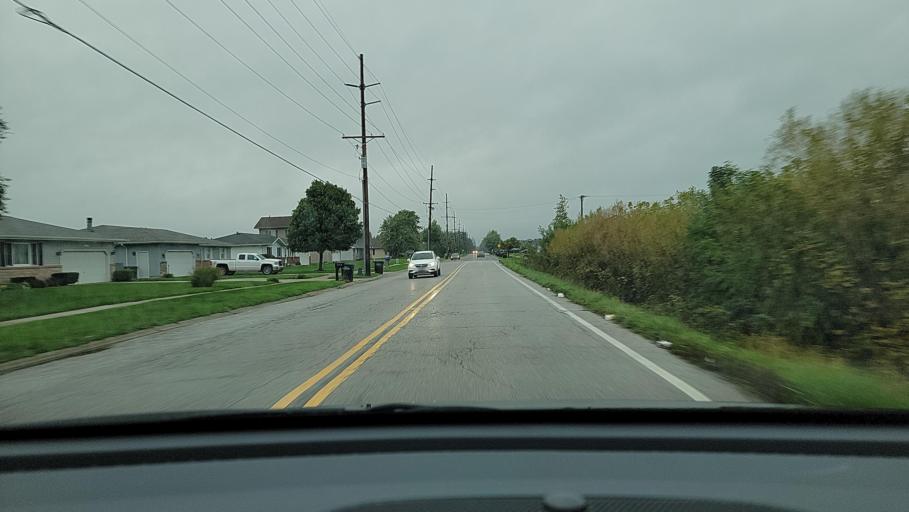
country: US
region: Indiana
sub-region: Porter County
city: Portage
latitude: 41.5606
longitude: -87.1634
